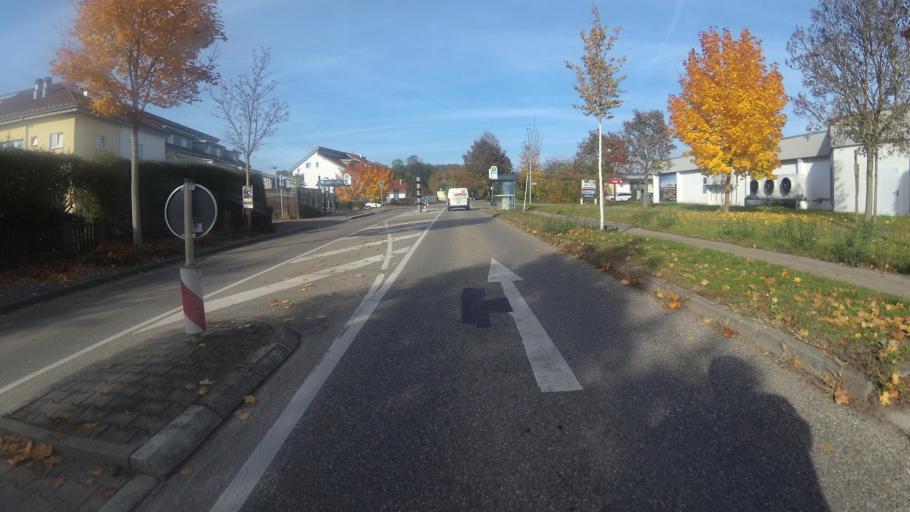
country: DE
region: Baden-Wuerttemberg
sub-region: Regierungsbezirk Stuttgart
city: Oedheim
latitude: 49.2452
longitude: 9.2450
